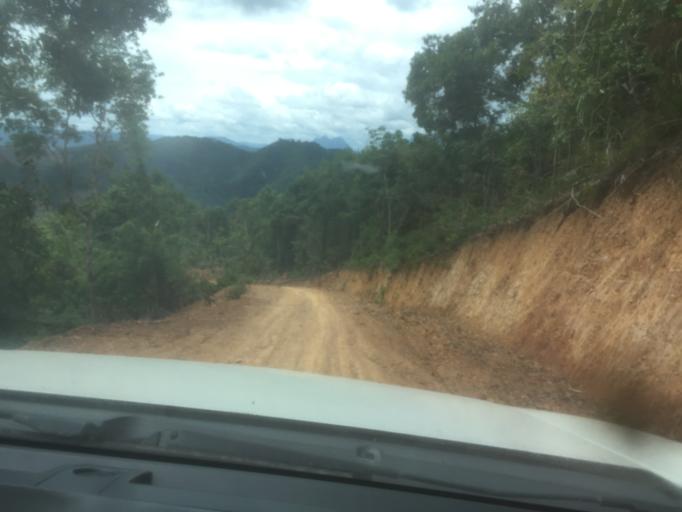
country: LA
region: Phongsali
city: Khoa
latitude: 20.9249
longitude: 102.5519
